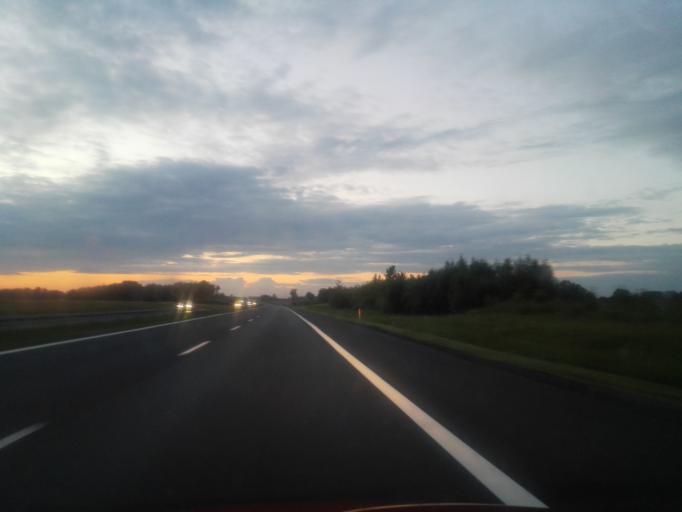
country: PL
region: Lodz Voivodeship
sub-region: Piotrkow Trybunalski
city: Piotrkow Trybunalski
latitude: 51.4463
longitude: 19.6422
